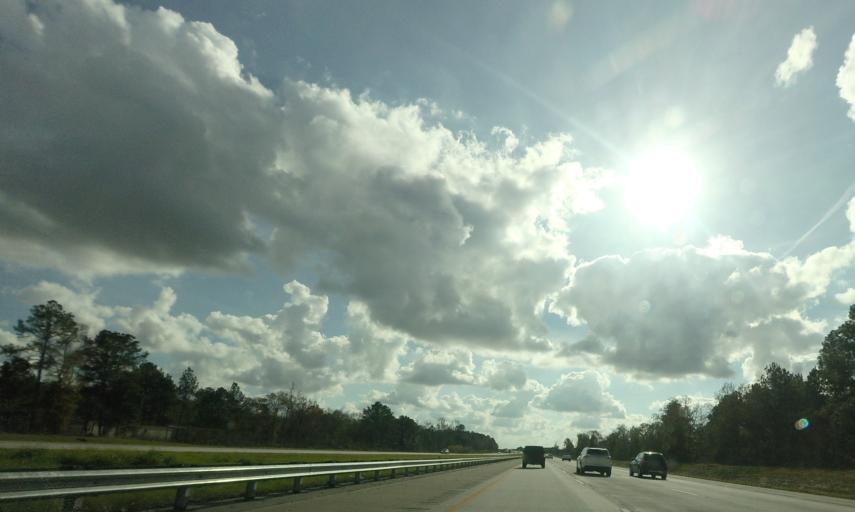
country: US
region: Georgia
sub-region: Dooly County
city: Unadilla
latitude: 32.2240
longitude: -83.7430
